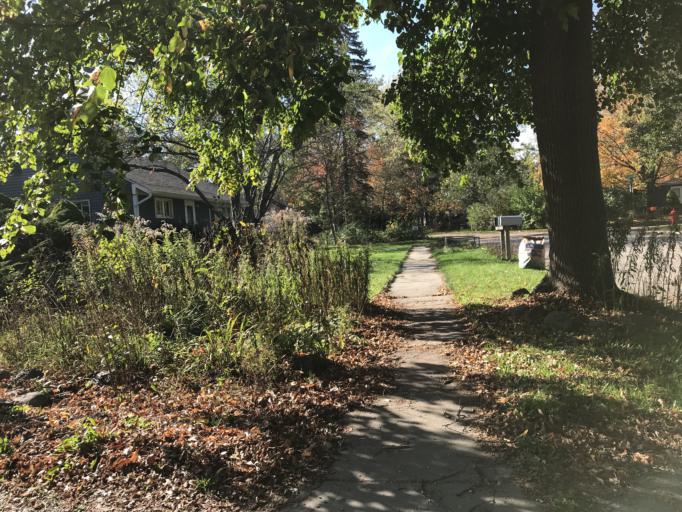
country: US
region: Michigan
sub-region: Washtenaw County
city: Ann Arbor
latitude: 42.2520
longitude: -83.7299
